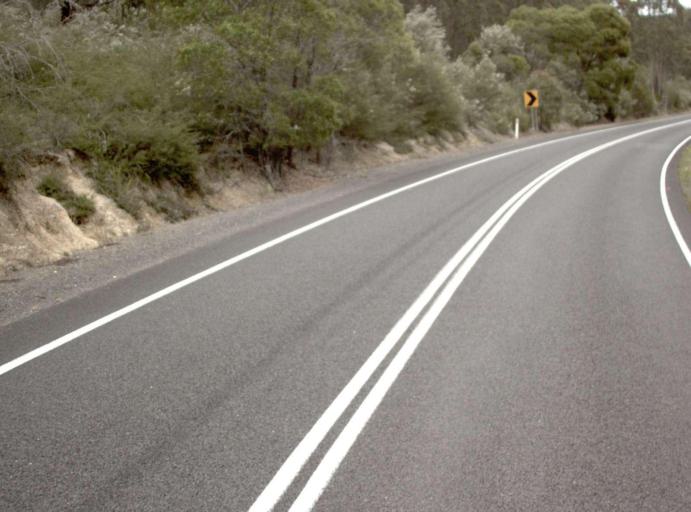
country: AU
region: New South Wales
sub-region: Bombala
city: Bombala
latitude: -37.2470
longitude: 149.2576
